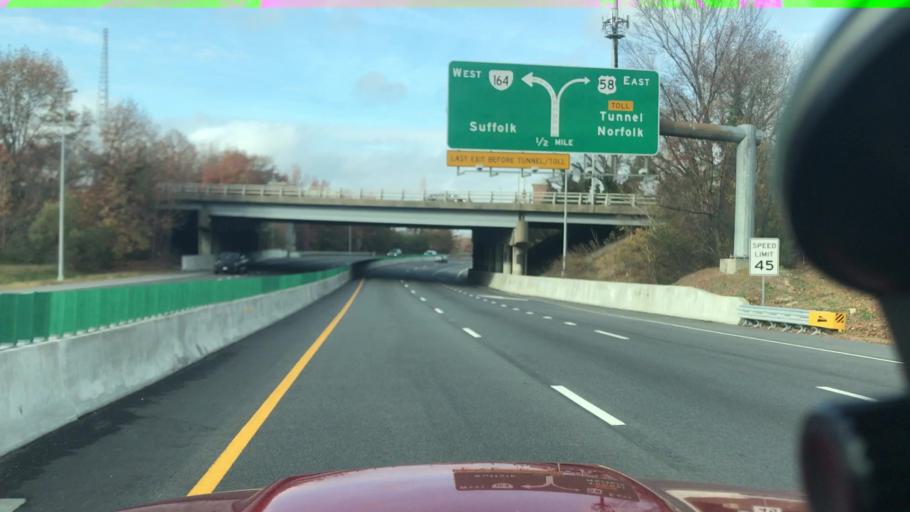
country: US
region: Virginia
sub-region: City of Portsmouth
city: Portsmouth
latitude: 36.8370
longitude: -76.3279
